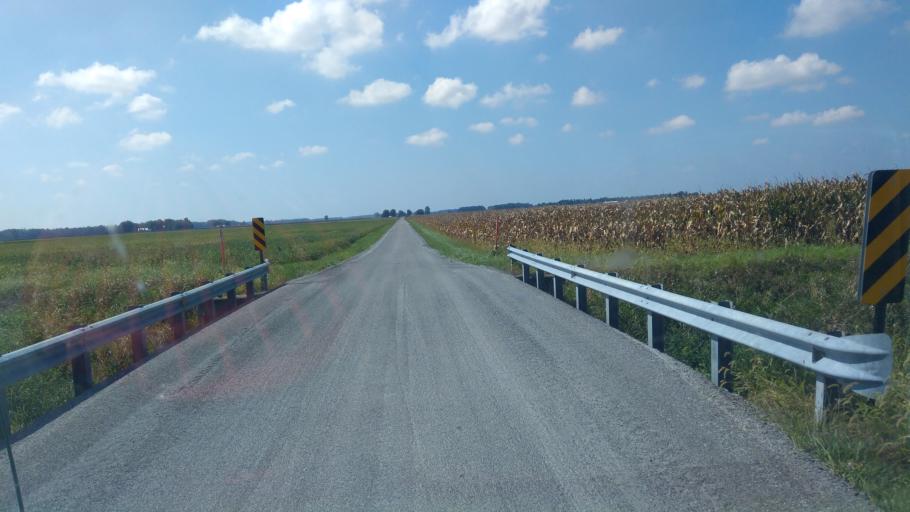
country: US
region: Ohio
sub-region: Hardin County
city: Ada
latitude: 40.7618
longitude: -83.7307
